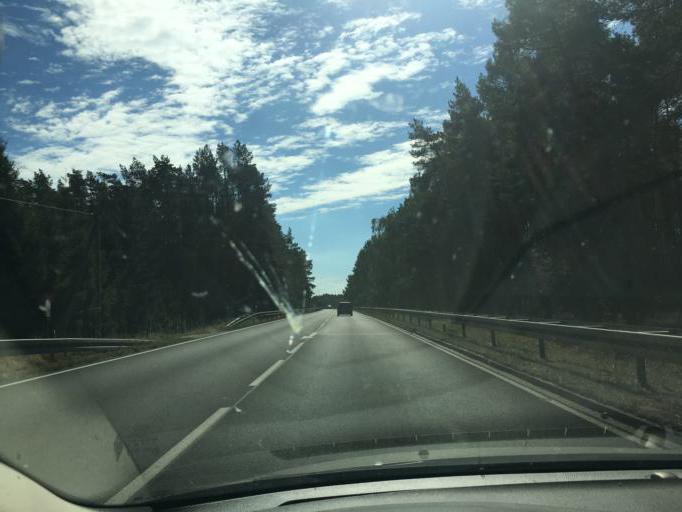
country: DE
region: Saxony-Anhalt
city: Seehausen
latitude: 52.8851
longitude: 11.7304
